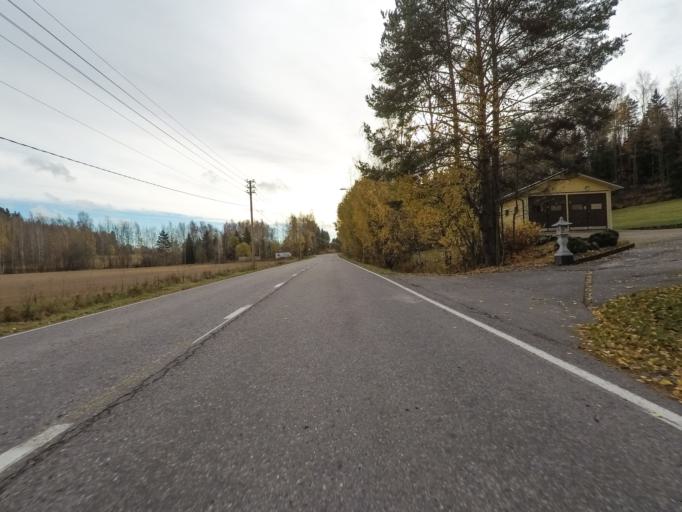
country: FI
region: Uusimaa
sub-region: Helsinki
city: Vantaa
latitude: 60.2659
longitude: 25.1395
